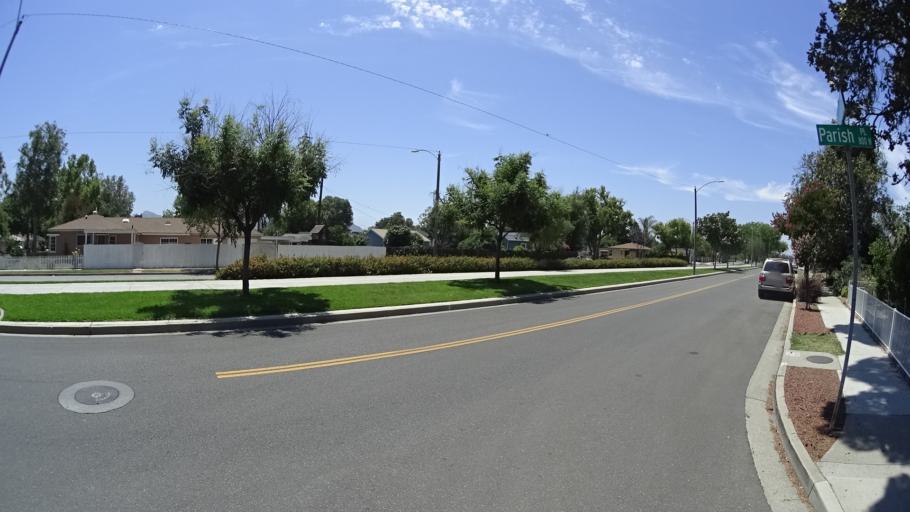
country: US
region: California
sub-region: Los Angeles County
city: Burbank
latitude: 34.1775
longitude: -118.3308
